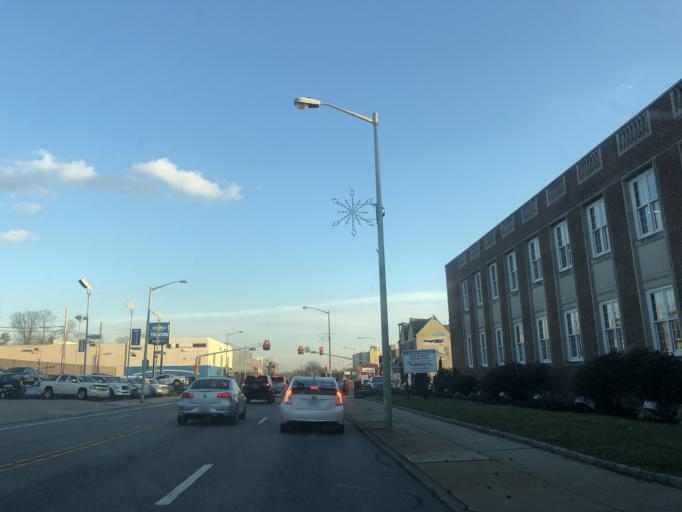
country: US
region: Pennsylvania
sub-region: Montgomery County
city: Ardmore
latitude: 40.0057
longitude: -75.2866
